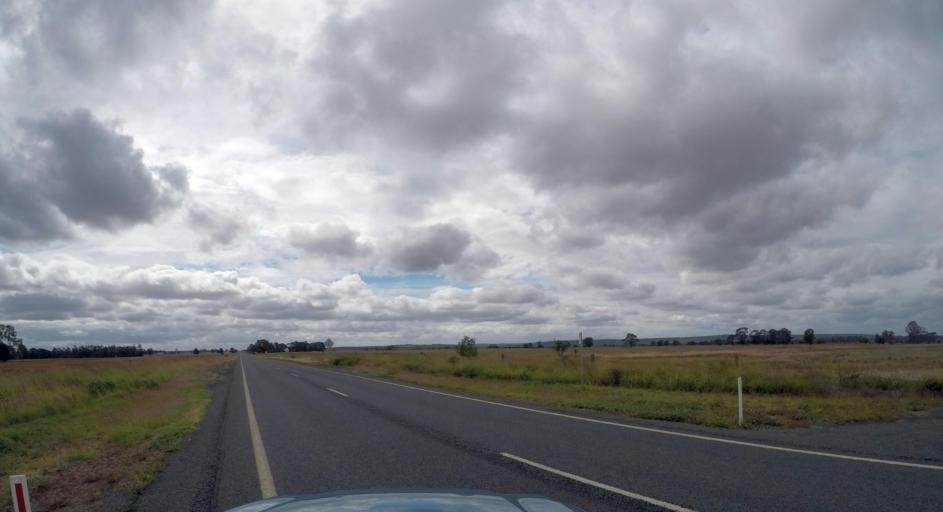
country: AU
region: Queensland
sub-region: South Burnett
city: Kingaroy
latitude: -26.3903
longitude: 151.2444
